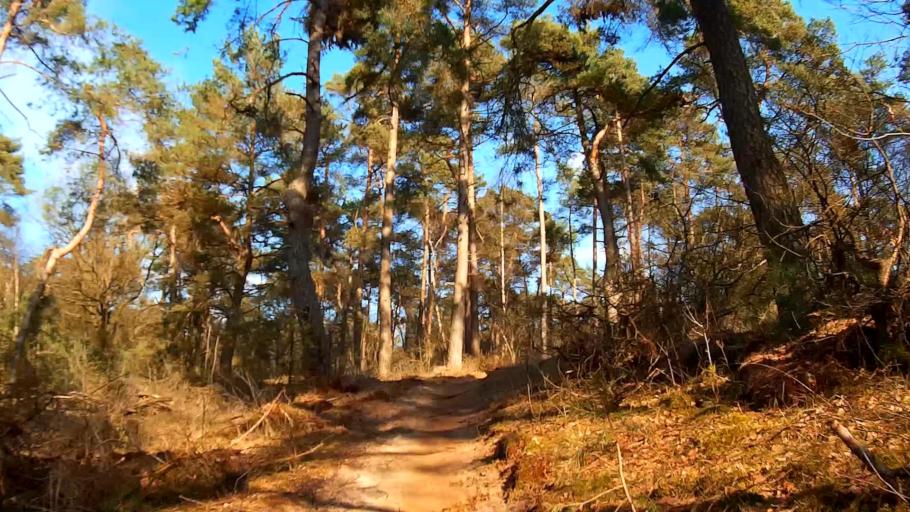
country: NL
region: Utrecht
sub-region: Gemeente Utrechtse Heuvelrug
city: Leersum
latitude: 52.0353
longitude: 5.4430
